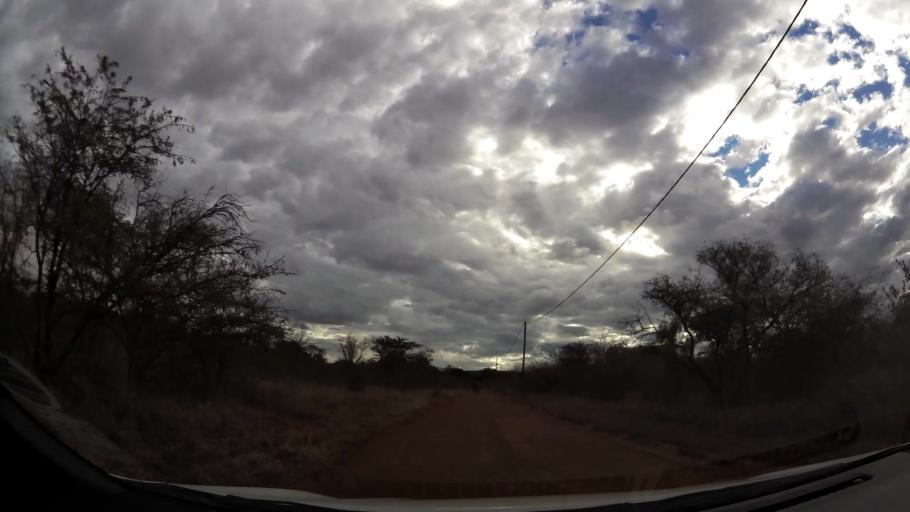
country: ZA
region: Limpopo
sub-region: Waterberg District Municipality
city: Modimolle
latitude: -24.5040
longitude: 28.7213
